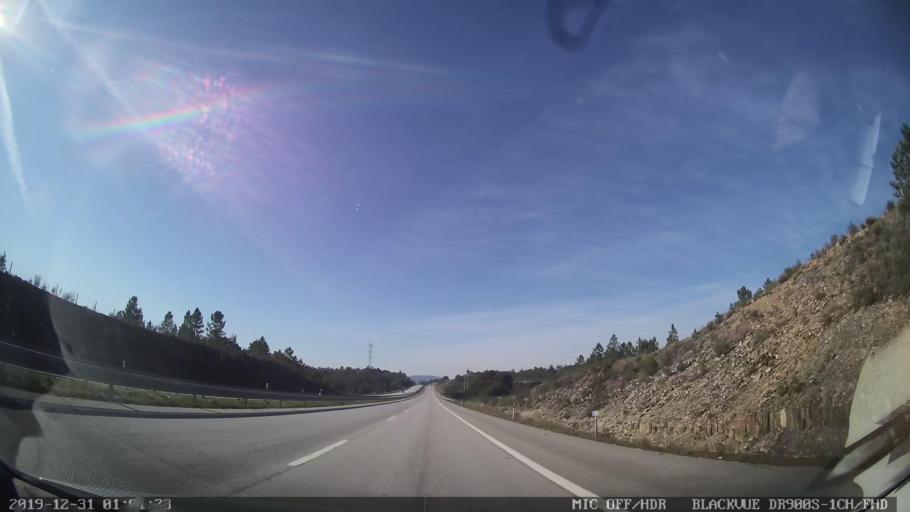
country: ES
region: Extremadura
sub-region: Provincia de Caceres
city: Cedillo
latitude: 39.7343
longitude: -7.6608
